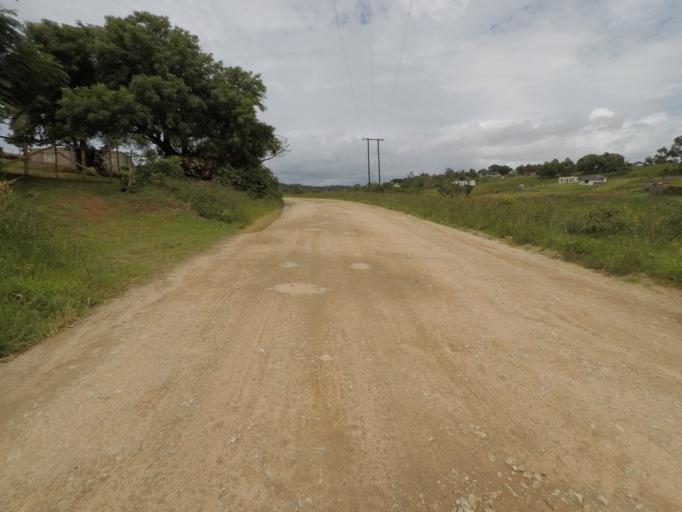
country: ZA
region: KwaZulu-Natal
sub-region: uThungulu District Municipality
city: eSikhawini
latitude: -28.9235
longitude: 31.8333
